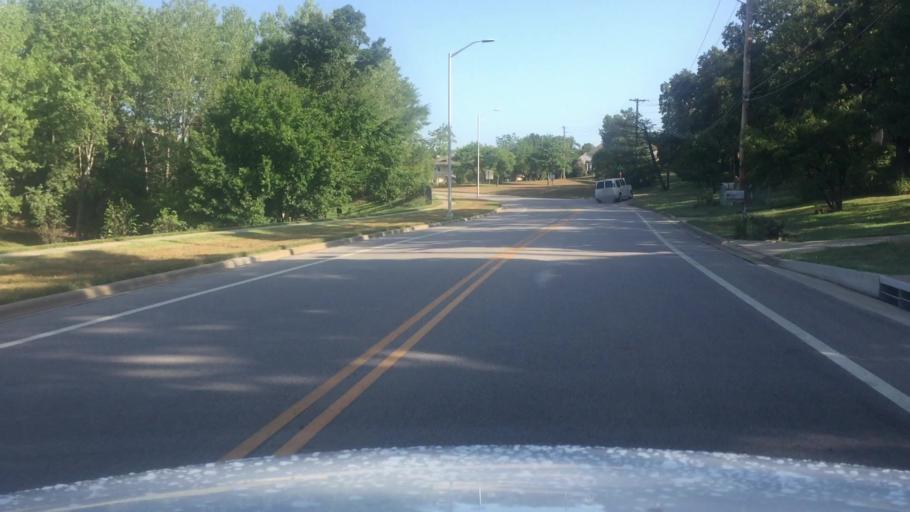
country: US
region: Kansas
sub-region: Johnson County
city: Shawnee
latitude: 39.0401
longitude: -94.7527
